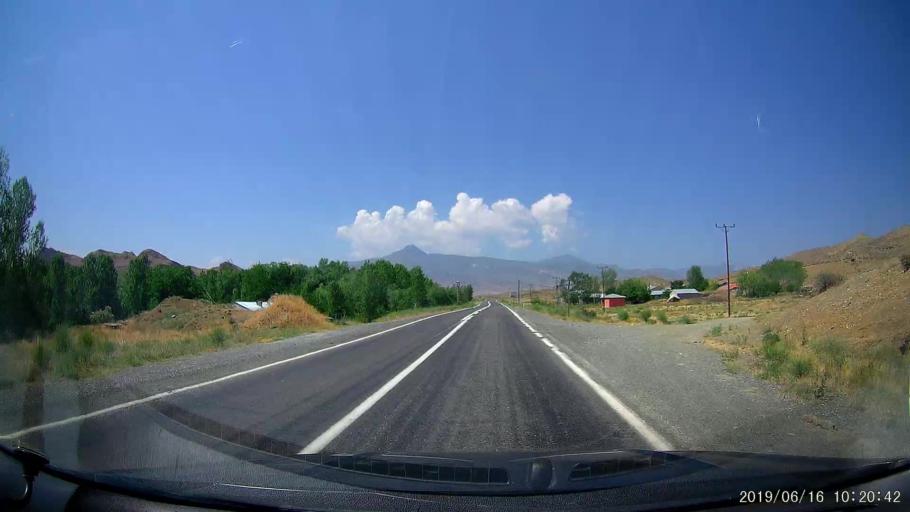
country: TR
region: Igdir
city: Tuzluca
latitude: 40.1453
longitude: 43.6449
